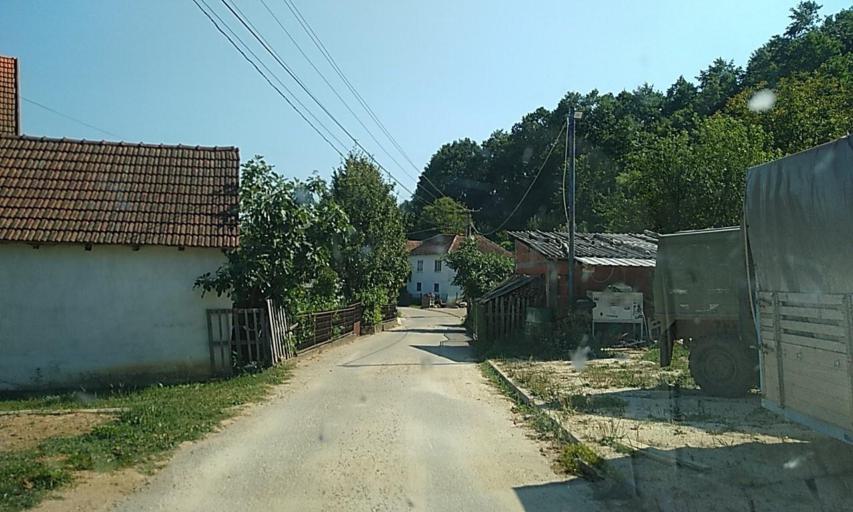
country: RS
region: Central Serbia
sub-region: Pcinjski Okrug
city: Vladicin Han
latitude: 42.7557
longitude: 22.0745
